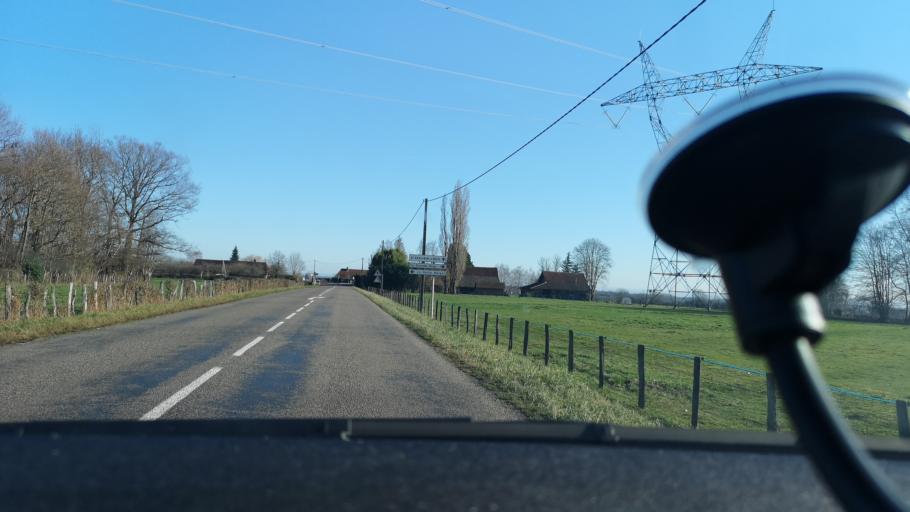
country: FR
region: Bourgogne
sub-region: Departement de Saone-et-Loire
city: Saint-Germain-du-Bois
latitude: 46.7478
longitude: 5.2107
